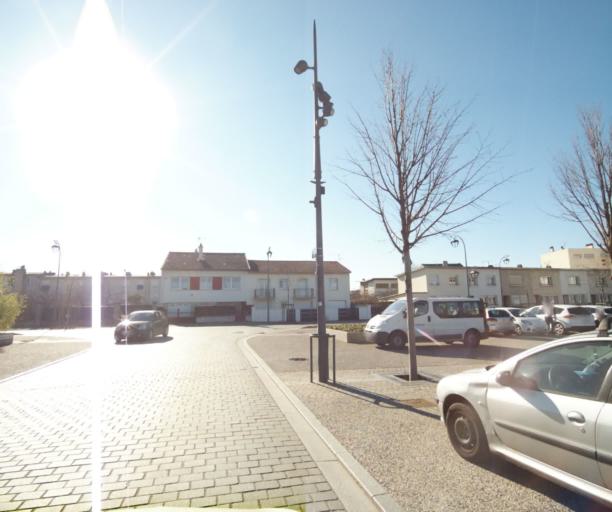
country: FR
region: Lorraine
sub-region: Departement de Meurthe-et-Moselle
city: Tomblaine
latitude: 48.6877
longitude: 6.2113
